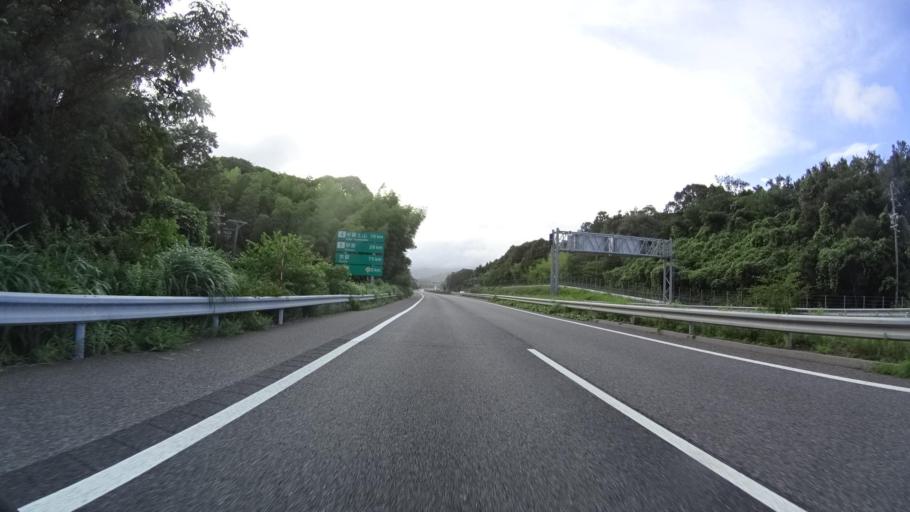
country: JP
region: Mie
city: Kameyama
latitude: 34.8989
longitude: 136.4480
